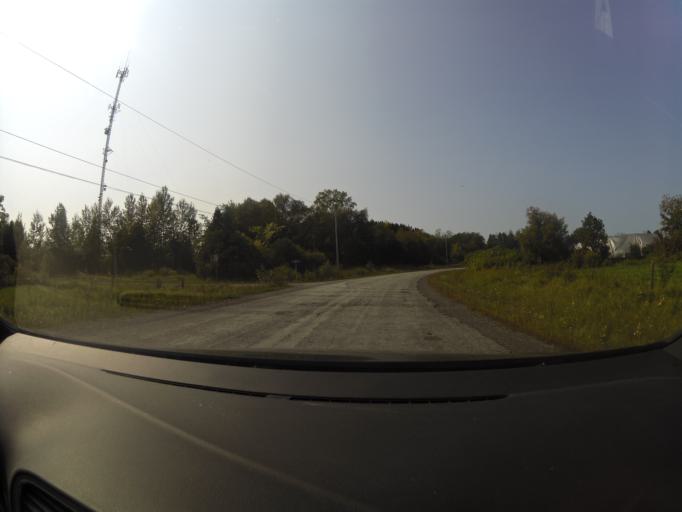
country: CA
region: Ontario
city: Carleton Place
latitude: 45.3235
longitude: -76.1023
